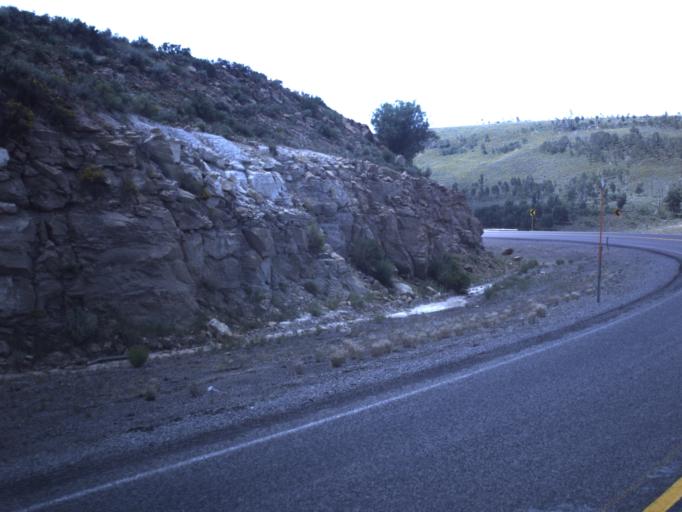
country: US
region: Utah
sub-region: Carbon County
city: Helper
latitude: 39.8306
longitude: -111.1385
